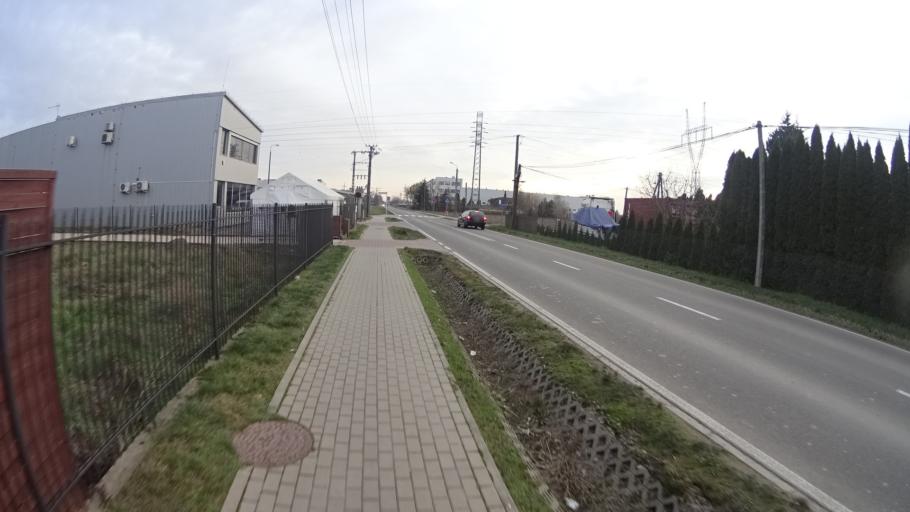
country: PL
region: Masovian Voivodeship
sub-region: Powiat warszawski zachodni
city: Babice
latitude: 52.2215
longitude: 20.8601
